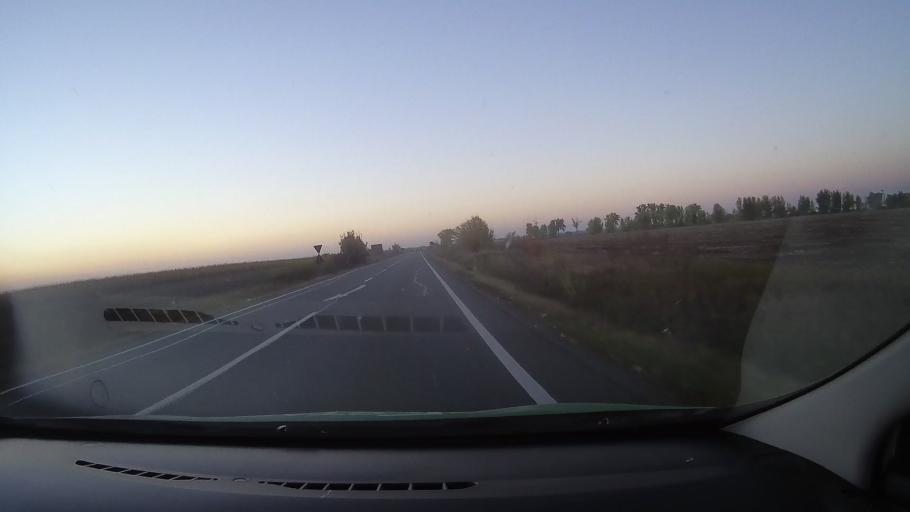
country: RO
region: Bihor
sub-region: Comuna Tarcea
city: Tarcea
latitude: 47.4312
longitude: 22.2069
